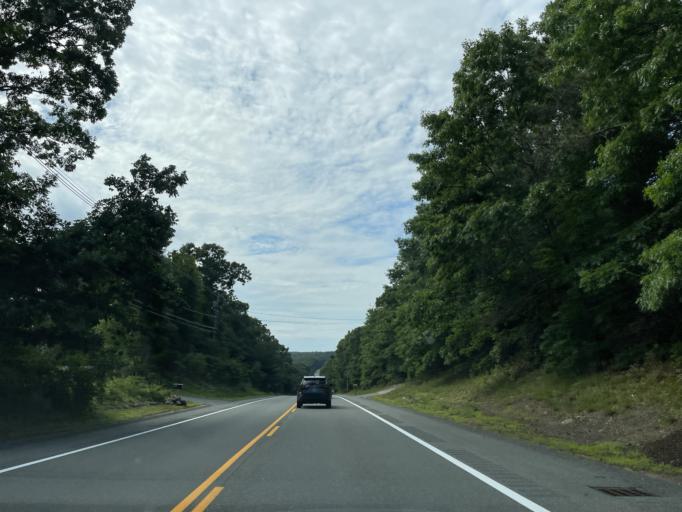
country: US
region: Rhode Island
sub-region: Kent County
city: West Greenwich
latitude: 41.6208
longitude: -71.6746
